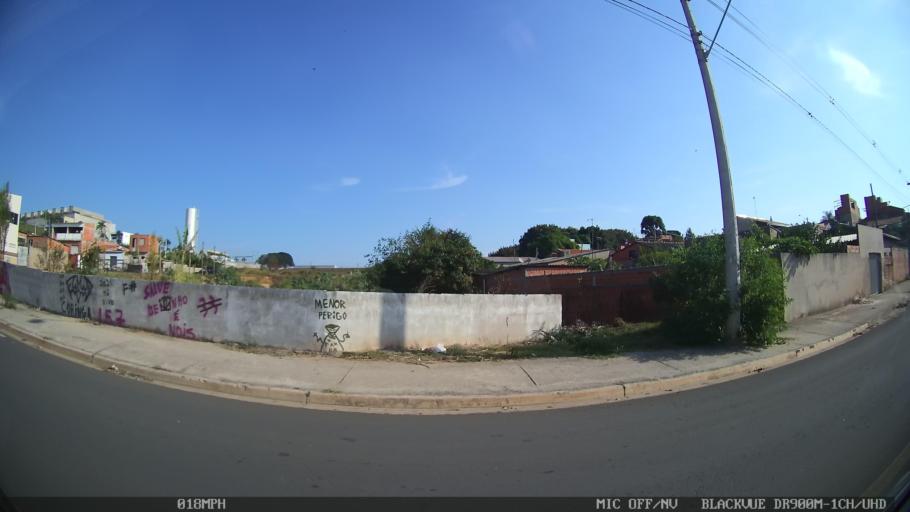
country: BR
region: Sao Paulo
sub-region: Campinas
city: Campinas
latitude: -22.9884
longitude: -47.1345
